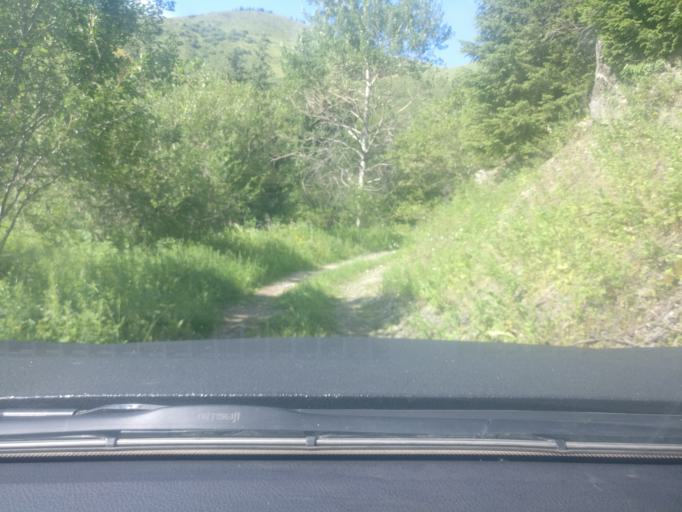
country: KZ
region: Almaty Qalasy
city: Almaty
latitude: 43.1043
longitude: 76.9513
